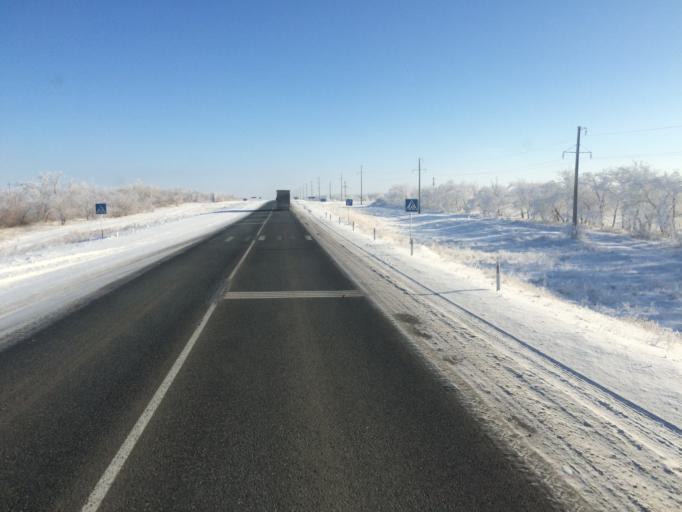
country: KZ
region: Aqtoebe
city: Aqtobe
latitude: 50.2472
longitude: 56.8072
